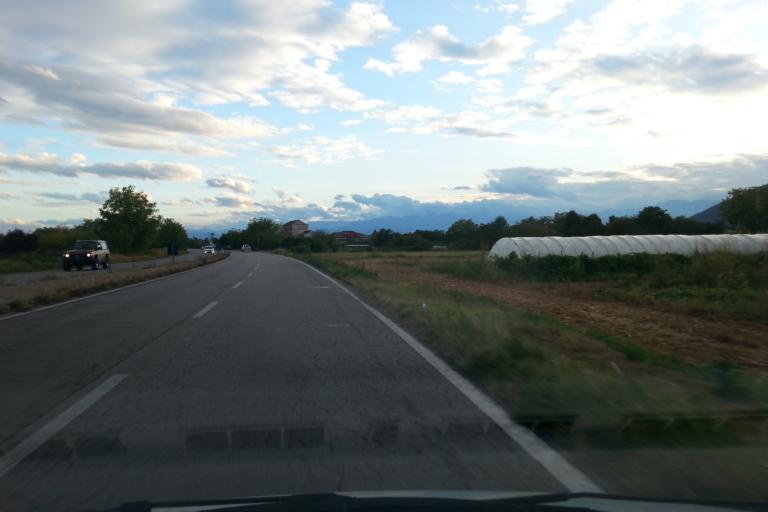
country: IT
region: Piedmont
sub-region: Provincia di Torino
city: Rivalta di Torino
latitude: 45.0170
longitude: 7.5240
